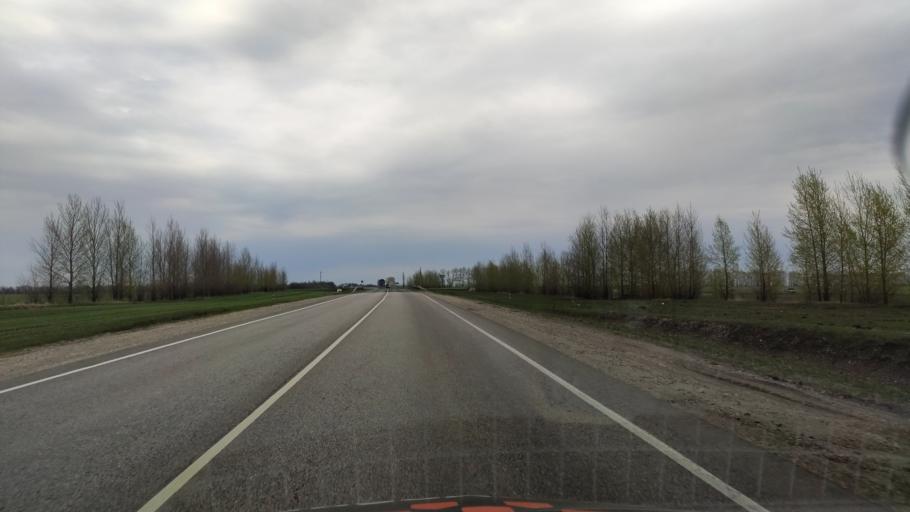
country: RU
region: Voronezj
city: Nizhnedevitsk
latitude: 51.5987
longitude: 38.5995
